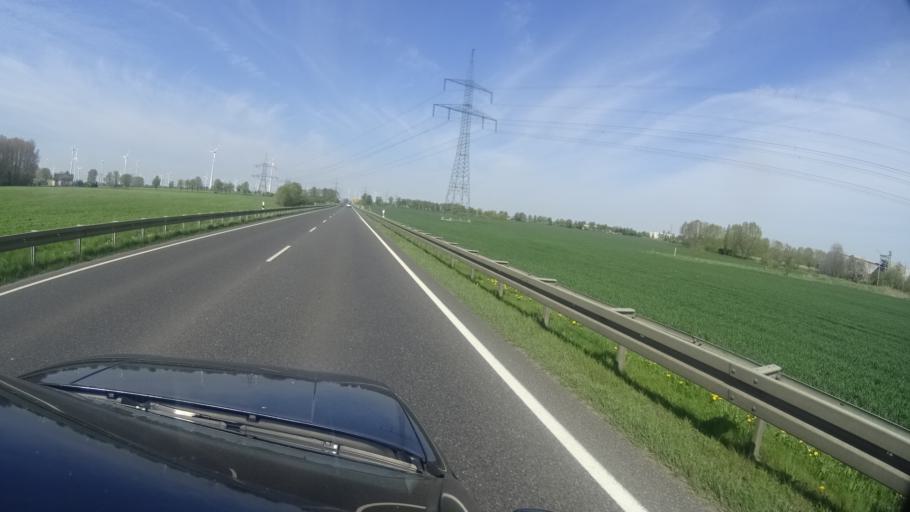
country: DE
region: Brandenburg
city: Nauen
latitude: 52.5927
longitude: 12.8820
